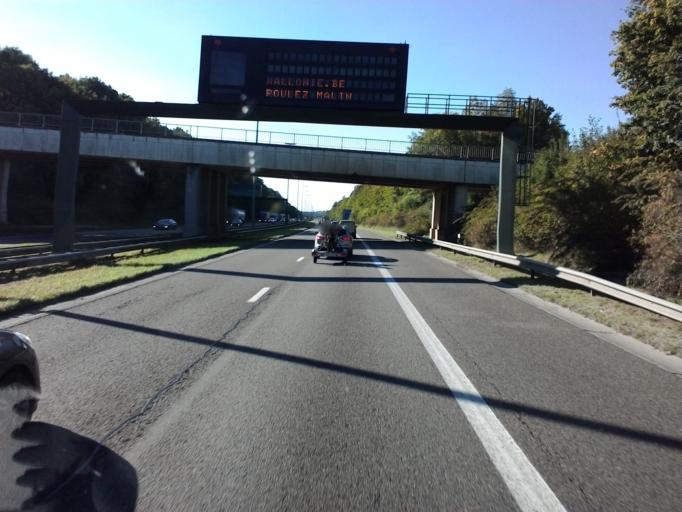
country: BE
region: Wallonia
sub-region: Province du Luxembourg
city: Arlon
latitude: 49.6683
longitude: 5.7999
